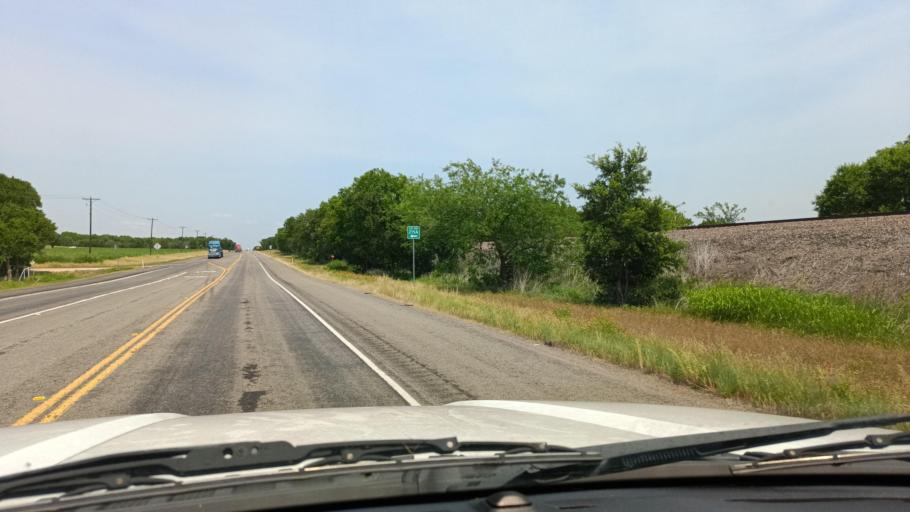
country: US
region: Texas
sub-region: Milam County
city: Cameron
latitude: 30.8486
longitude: -97.0333
